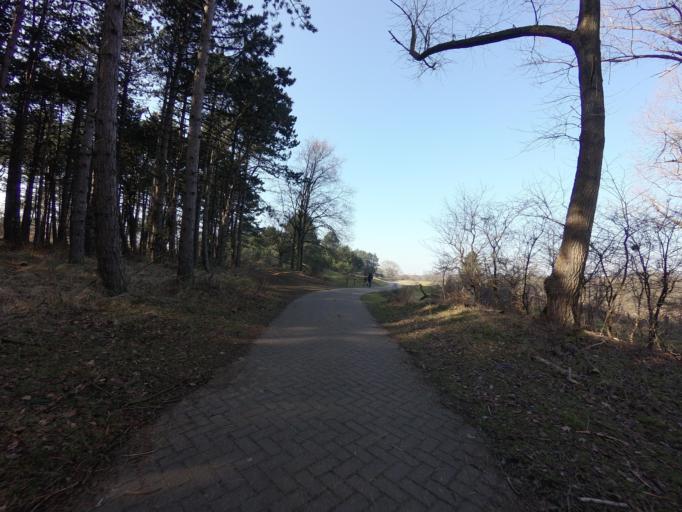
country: NL
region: North Holland
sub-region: Gemeente Bloemendaal
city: Bloemendaal
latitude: 52.4387
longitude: 4.6115
